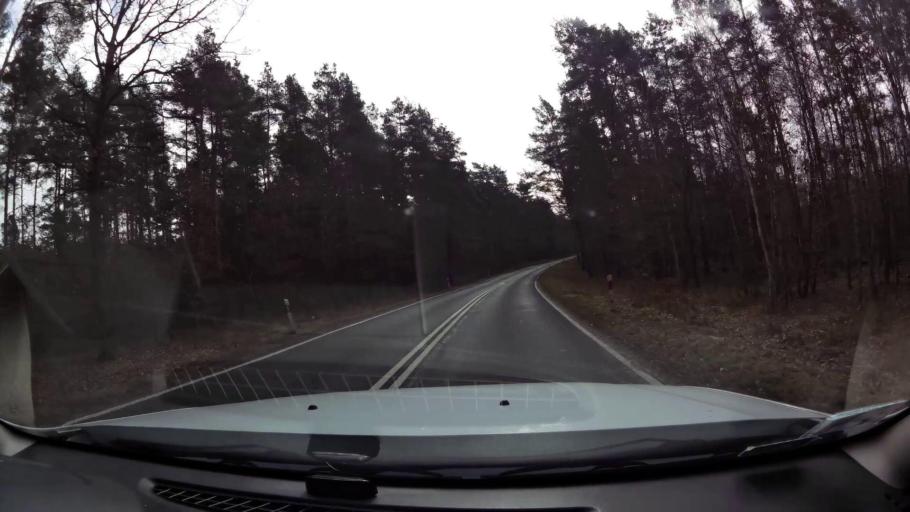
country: PL
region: West Pomeranian Voivodeship
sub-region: Powiat mysliborski
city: Debno
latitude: 52.7667
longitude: 14.6757
